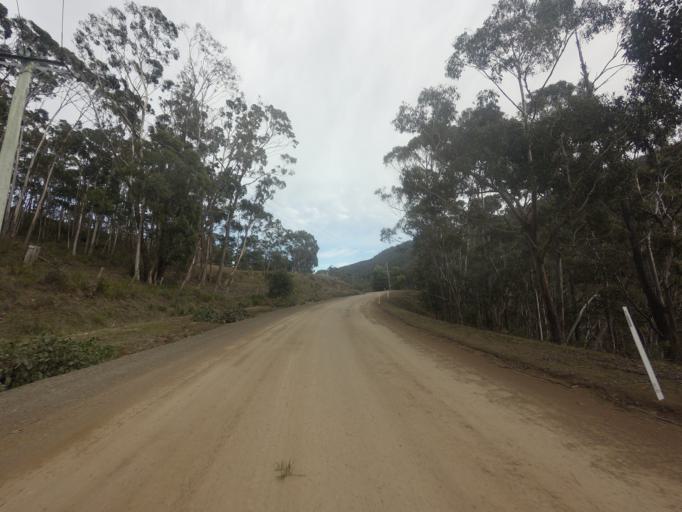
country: AU
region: Tasmania
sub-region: Huon Valley
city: Huonville
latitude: -43.0526
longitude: 147.1060
